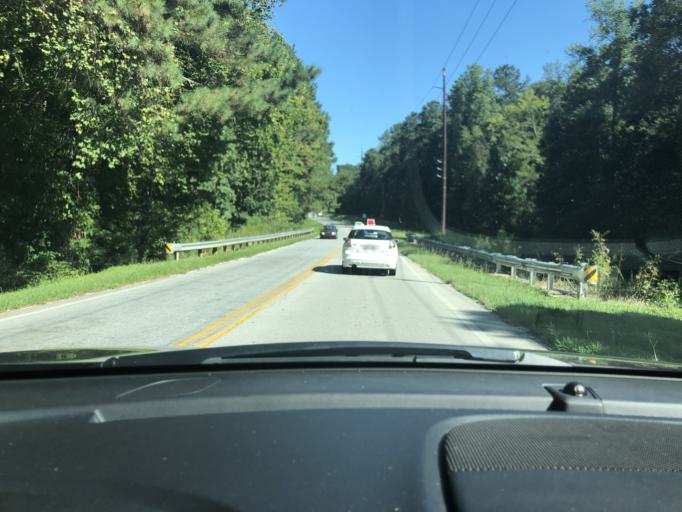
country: US
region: Georgia
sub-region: Gwinnett County
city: Grayson
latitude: 33.9197
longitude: -83.9428
